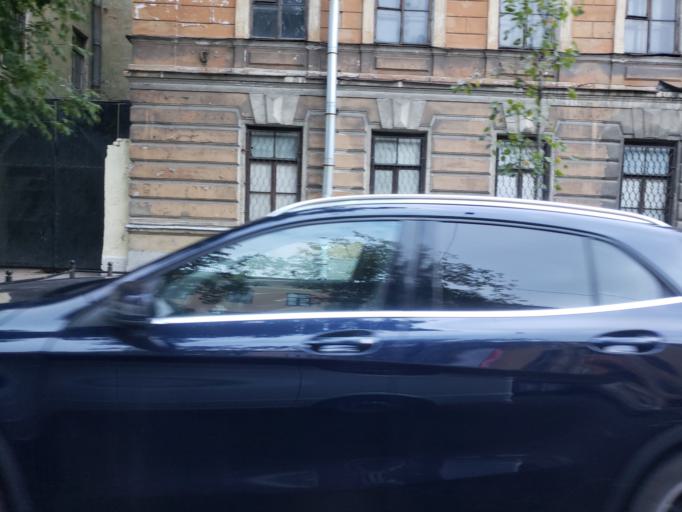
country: RU
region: St.-Petersburg
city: Vasyl'evsky Ostrov
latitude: 59.9359
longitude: 30.2770
